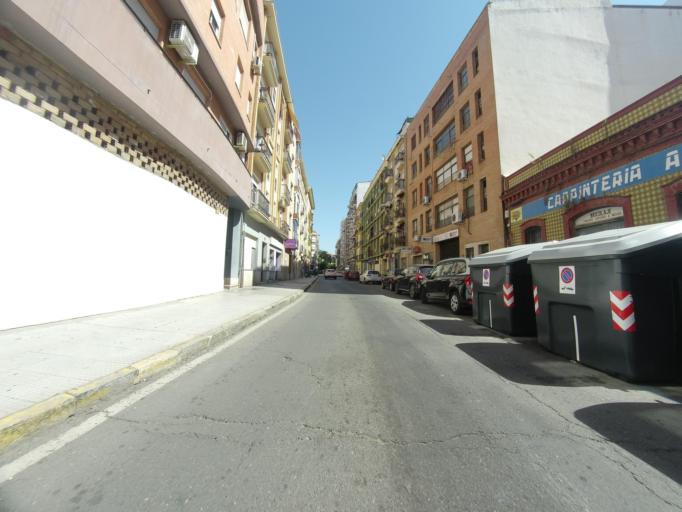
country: ES
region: Andalusia
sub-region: Provincia de Huelva
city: Huelva
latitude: 37.2613
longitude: -6.9537
